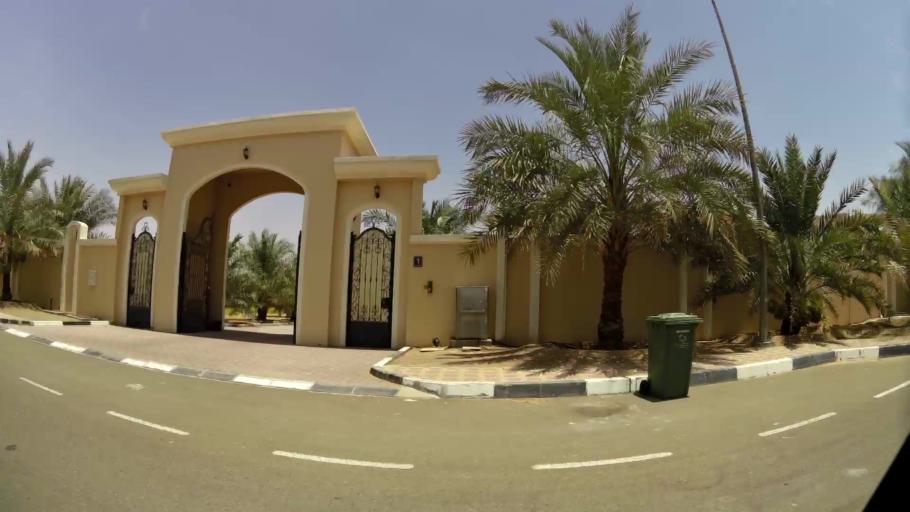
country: OM
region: Al Buraimi
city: Al Buraymi
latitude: 24.2862
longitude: 55.7358
